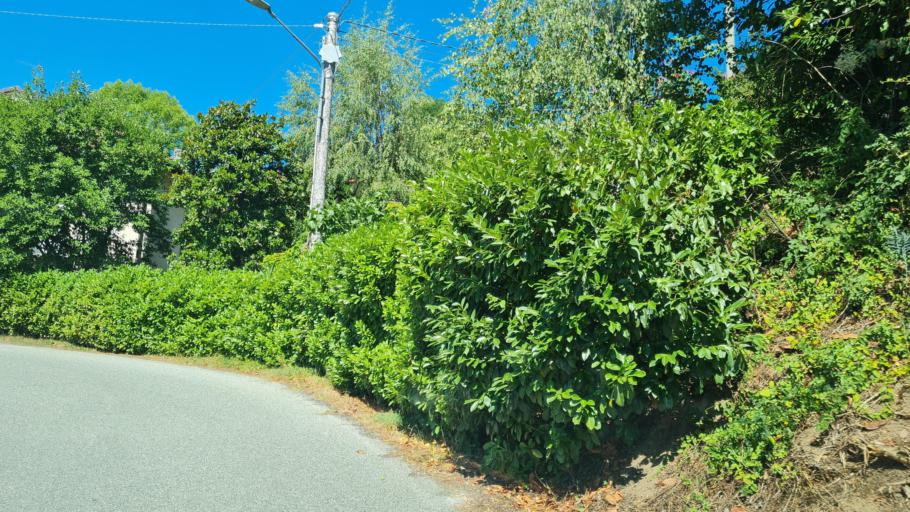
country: IT
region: Piedmont
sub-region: Provincia di Biella
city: Masserano
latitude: 45.5988
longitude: 8.2104
